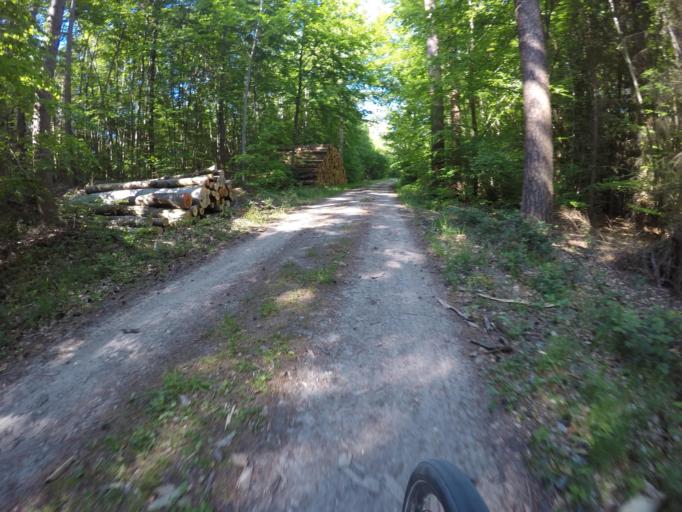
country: DE
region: Baden-Wuerttemberg
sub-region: Regierungsbezirk Stuttgart
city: Sindelfingen
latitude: 48.7432
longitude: 9.0464
